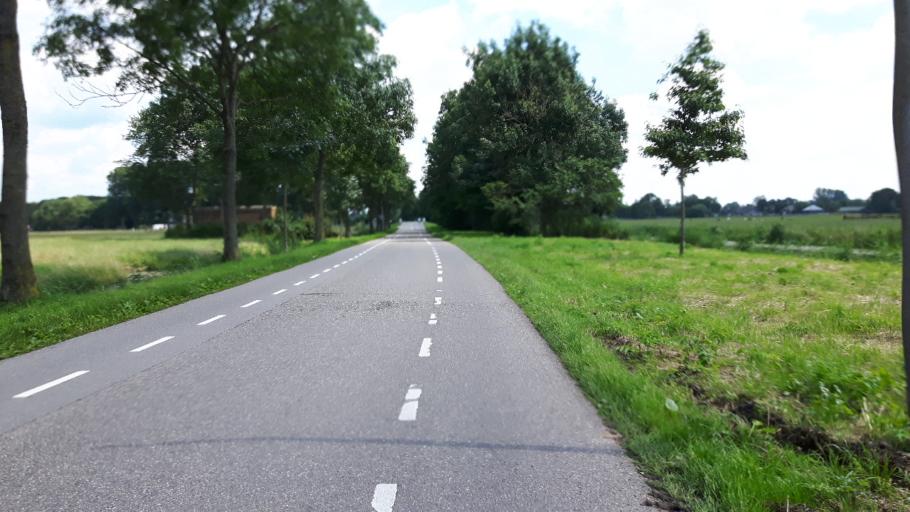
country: NL
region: South Holland
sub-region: Bodegraven-Reeuwijk
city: Bodegraven
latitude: 52.0815
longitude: 4.7283
